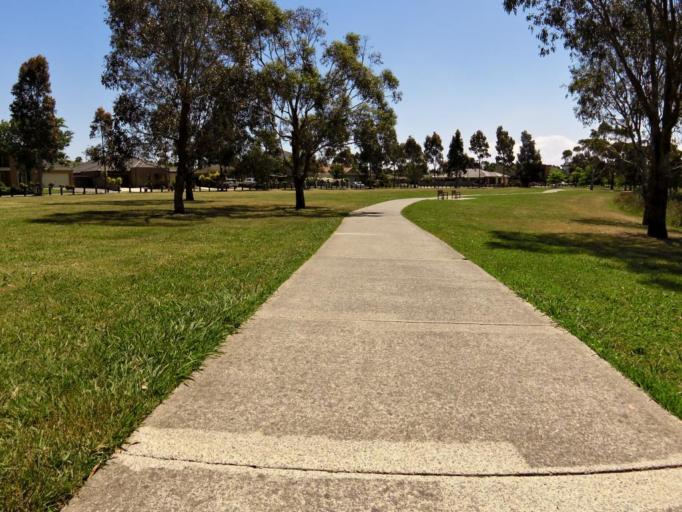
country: AU
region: Victoria
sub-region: Casey
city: Narre Warren South
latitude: -38.0629
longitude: 145.3238
